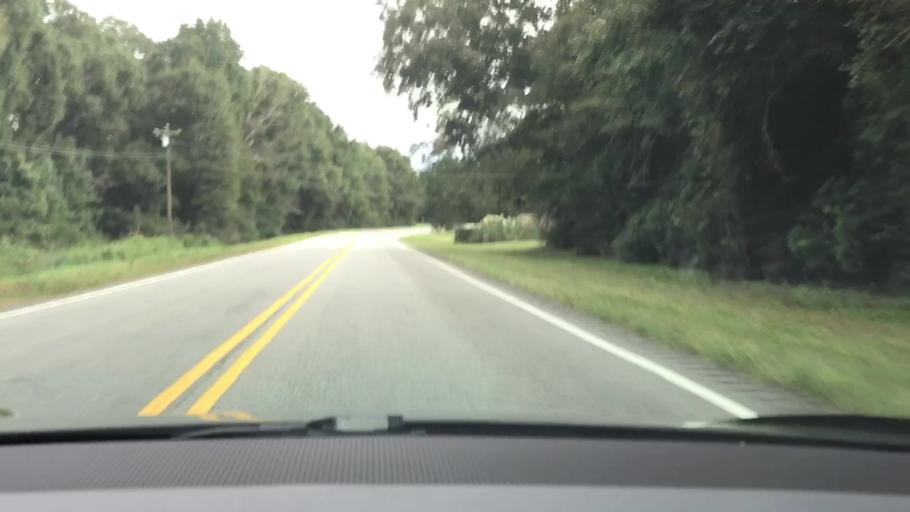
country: US
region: Alabama
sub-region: Coffee County
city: Elba
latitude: 31.5801
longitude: -85.9980
